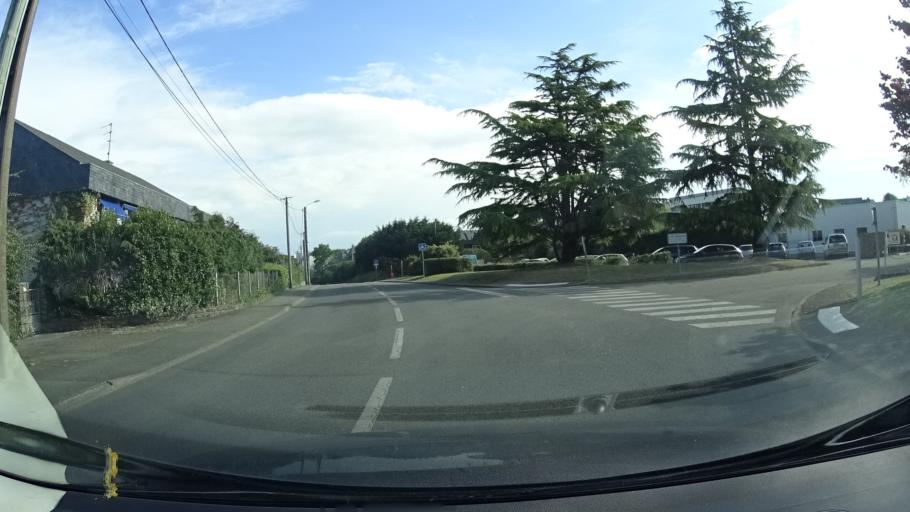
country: FR
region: Brittany
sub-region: Departement du Morbihan
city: Vannes
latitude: 47.6456
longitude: -2.7580
